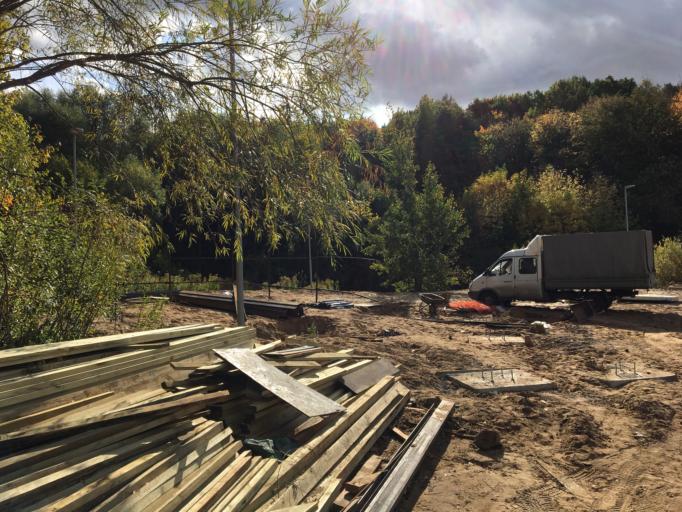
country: RU
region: Nizjnij Novgorod
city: Nizhniy Novgorod
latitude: 56.2702
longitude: 44.0066
